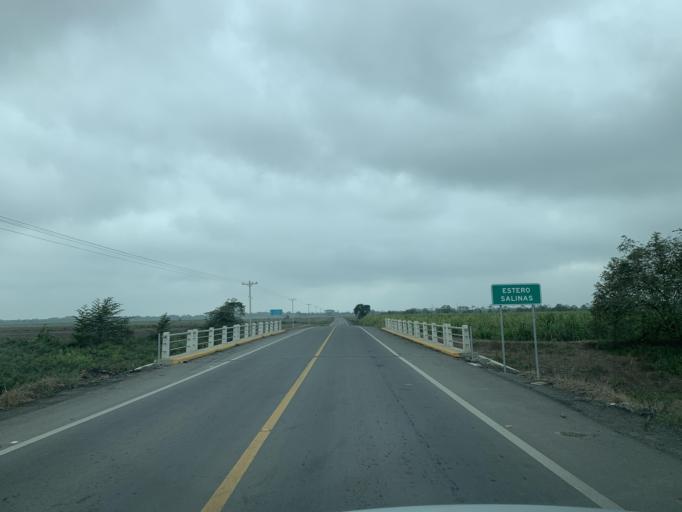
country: EC
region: Guayas
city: Coronel Marcelino Mariduena
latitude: -2.3129
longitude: -79.5125
